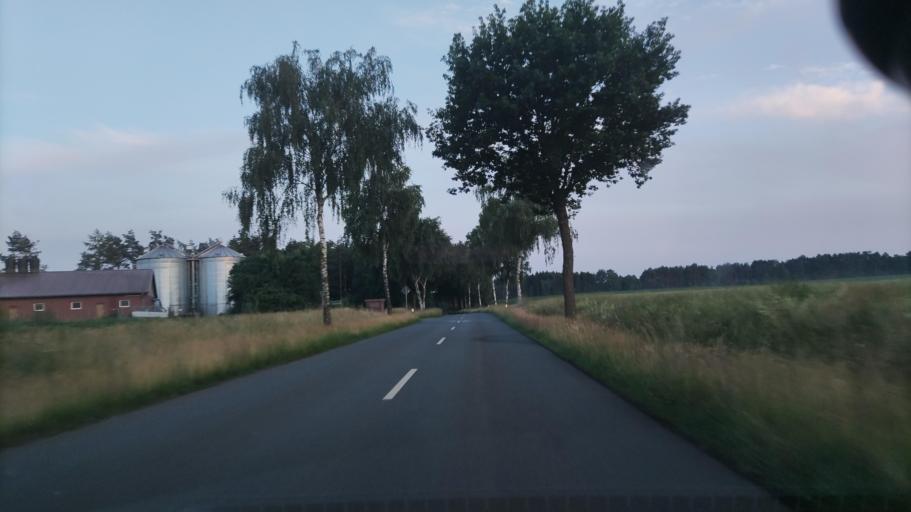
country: DE
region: Lower Saxony
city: Bispingen
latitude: 53.1142
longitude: 10.0575
